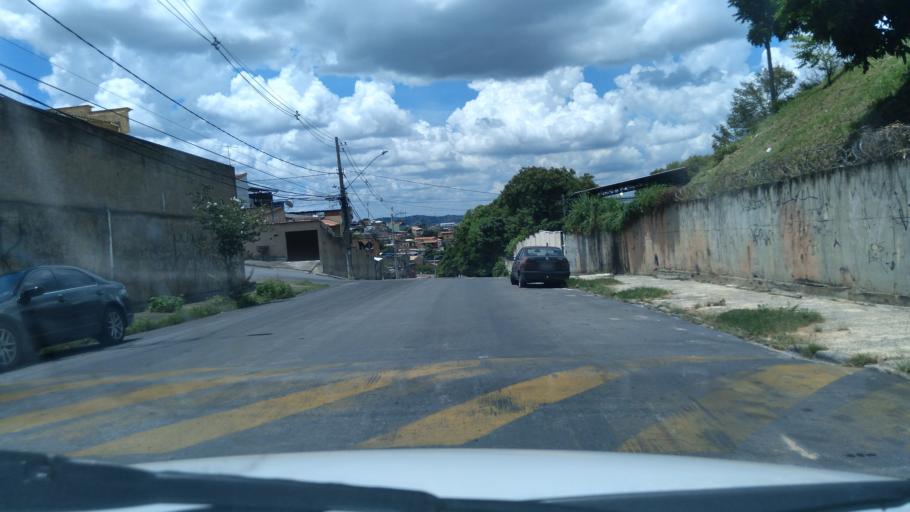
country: BR
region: Minas Gerais
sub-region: Belo Horizonte
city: Belo Horizonte
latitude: -19.8861
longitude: -43.8939
